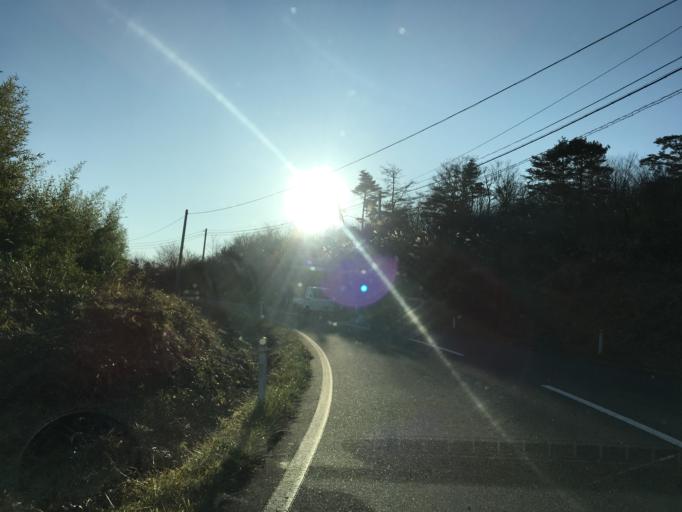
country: JP
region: Iwate
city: Ichinoseki
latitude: 38.7850
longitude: 141.2233
